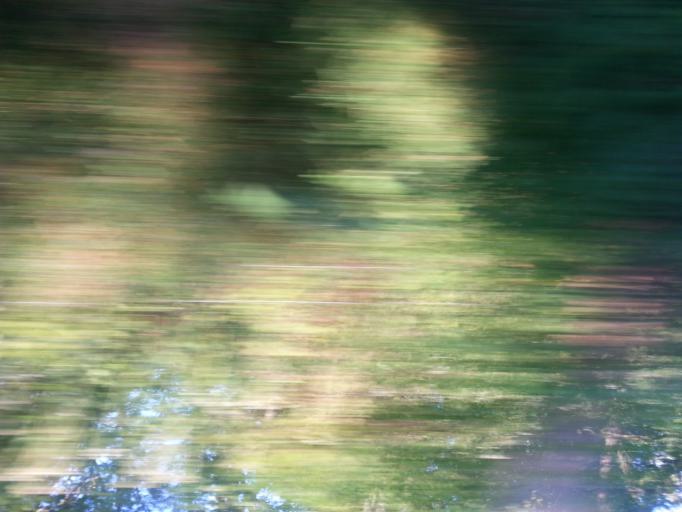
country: US
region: Tennessee
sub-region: Blount County
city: Wildwood
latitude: 35.8269
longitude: -83.8938
